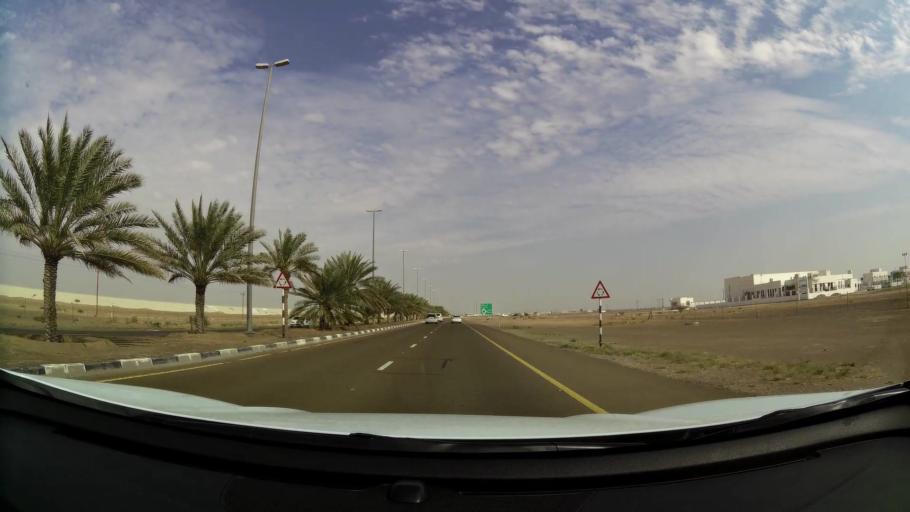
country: AE
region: Abu Dhabi
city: Al Ain
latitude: 24.0925
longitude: 55.8708
